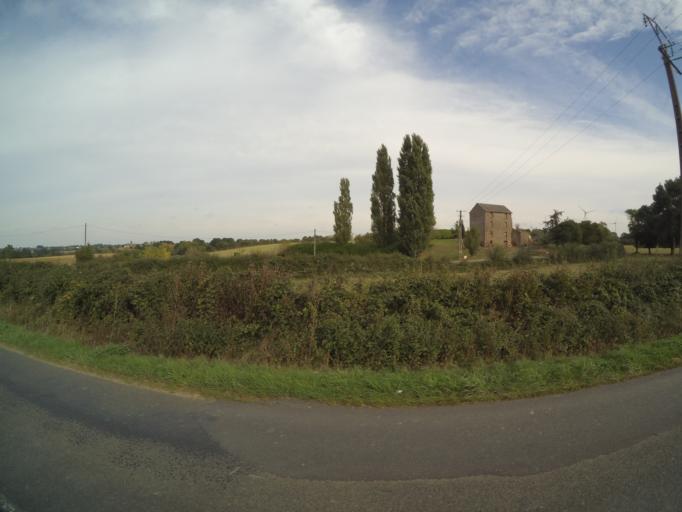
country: FR
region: Pays de la Loire
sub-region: Departement de Maine-et-Loire
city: Vihiers
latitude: 47.2078
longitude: -0.5780
